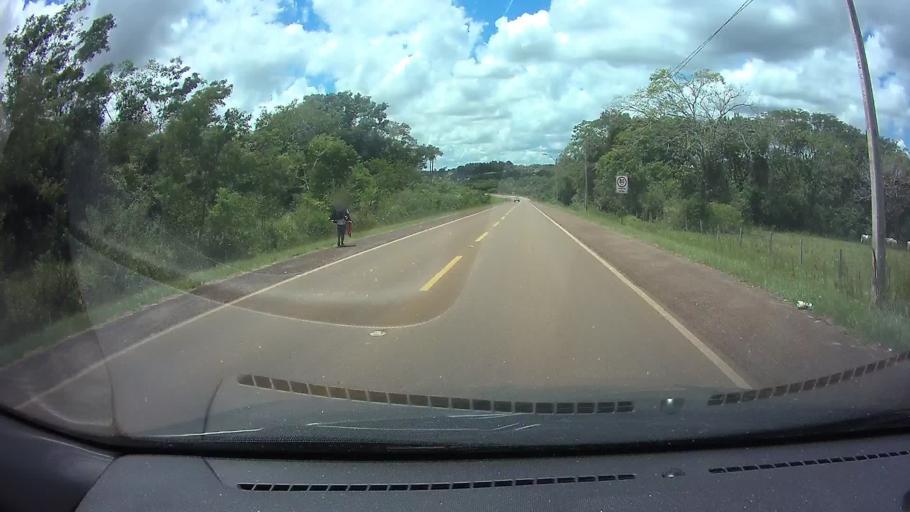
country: PY
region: Paraguari
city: La Colmena
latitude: -25.8929
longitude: -56.8364
